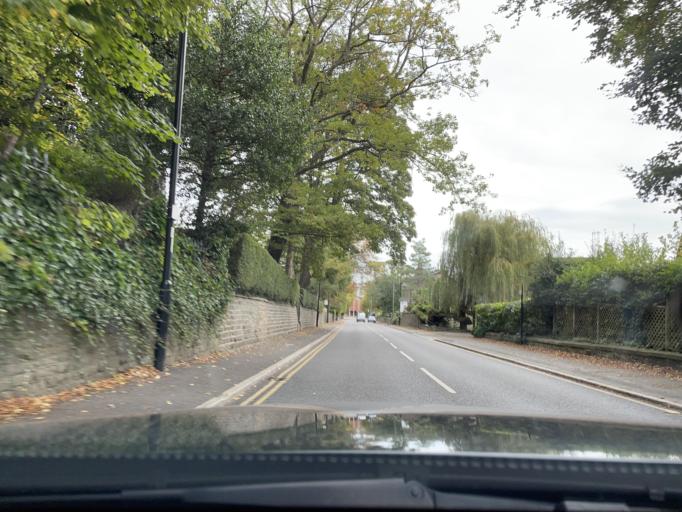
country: GB
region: England
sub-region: Sheffield
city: Sheffield
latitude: 53.3767
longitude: -1.5075
